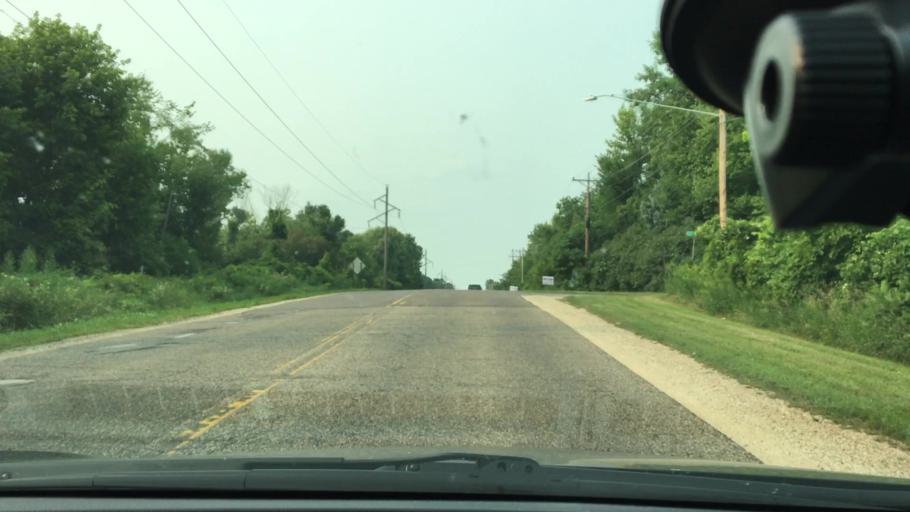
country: US
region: Minnesota
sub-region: Hennepin County
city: Champlin
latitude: 45.1894
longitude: -93.4424
